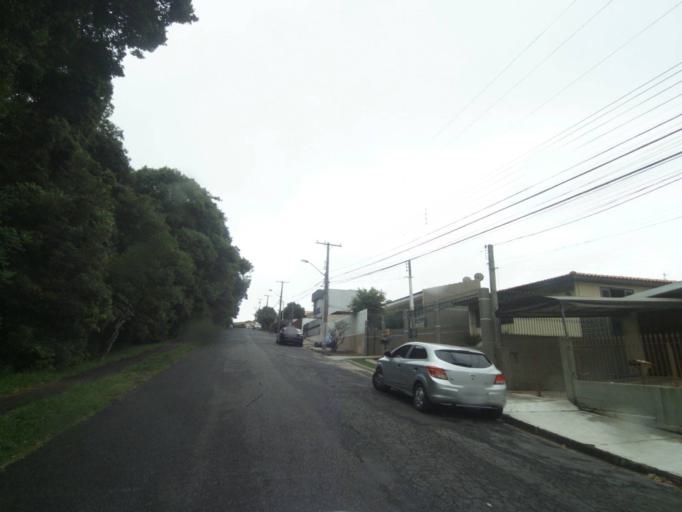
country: BR
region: Parana
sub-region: Curitiba
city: Curitiba
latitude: -25.4282
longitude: -49.3423
